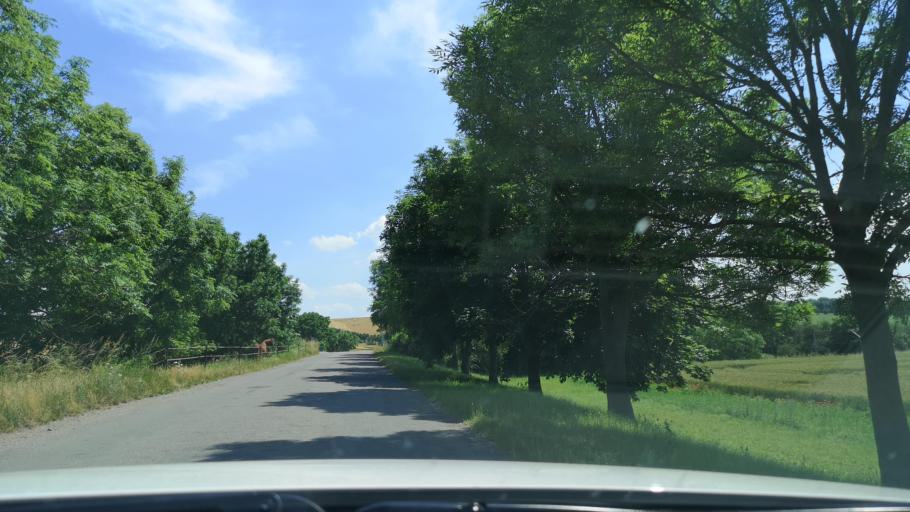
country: DE
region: Thuringia
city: Eberstedt
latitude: 51.0594
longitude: 11.5680
